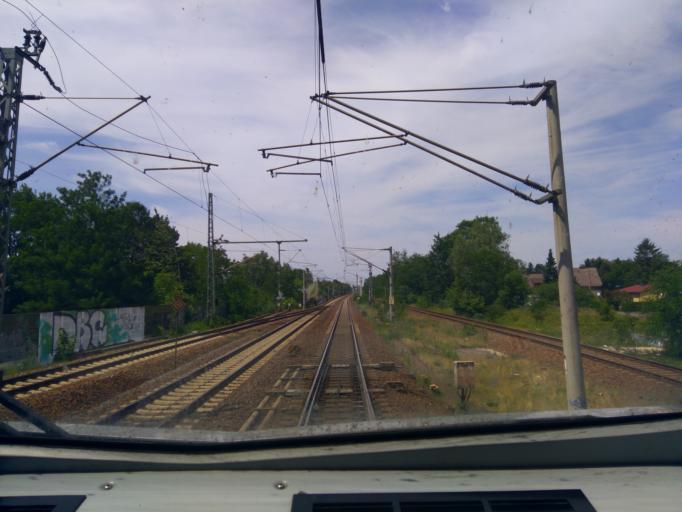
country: DE
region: Brandenburg
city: Brieselang
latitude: 52.5856
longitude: 12.9895
